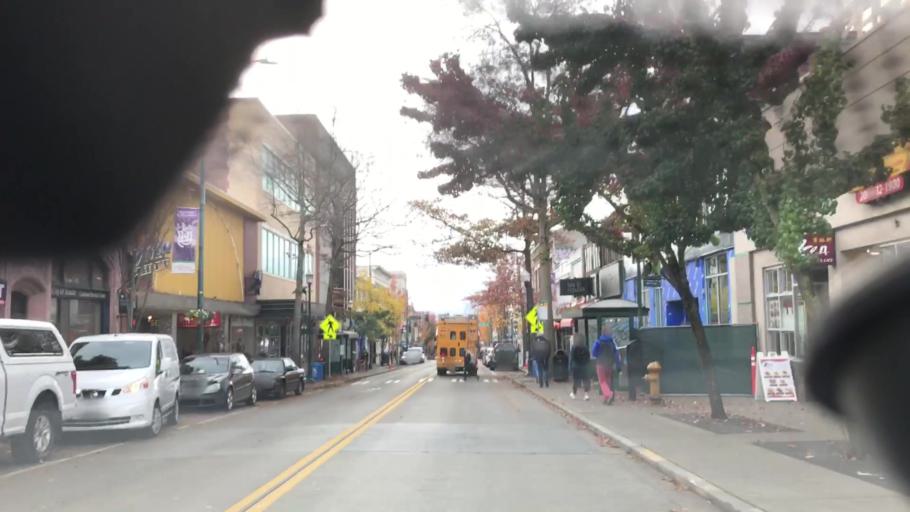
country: US
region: Washington
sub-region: King County
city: Seattle
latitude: 47.6626
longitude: -122.3131
